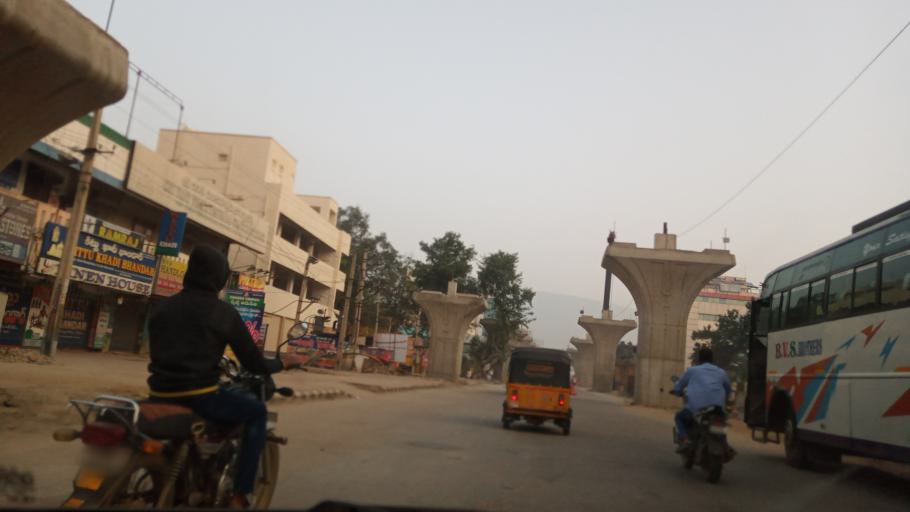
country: IN
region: Andhra Pradesh
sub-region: Chittoor
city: Tirupati
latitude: 13.6330
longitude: 79.4279
